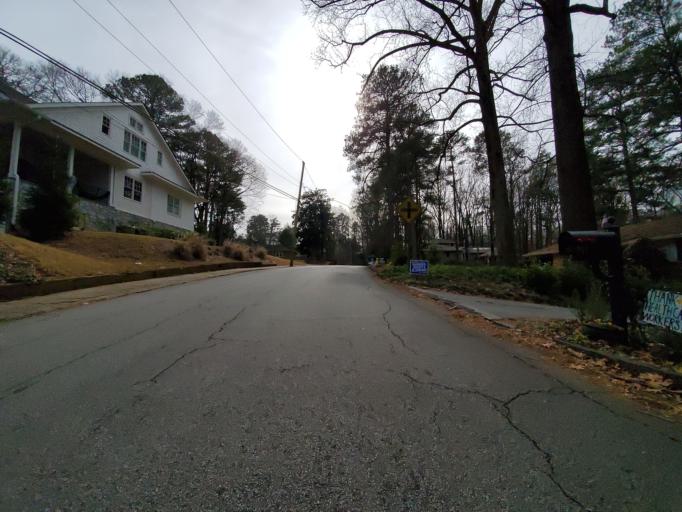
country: US
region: Georgia
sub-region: DeKalb County
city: North Decatur
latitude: 33.7829
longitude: -84.3171
